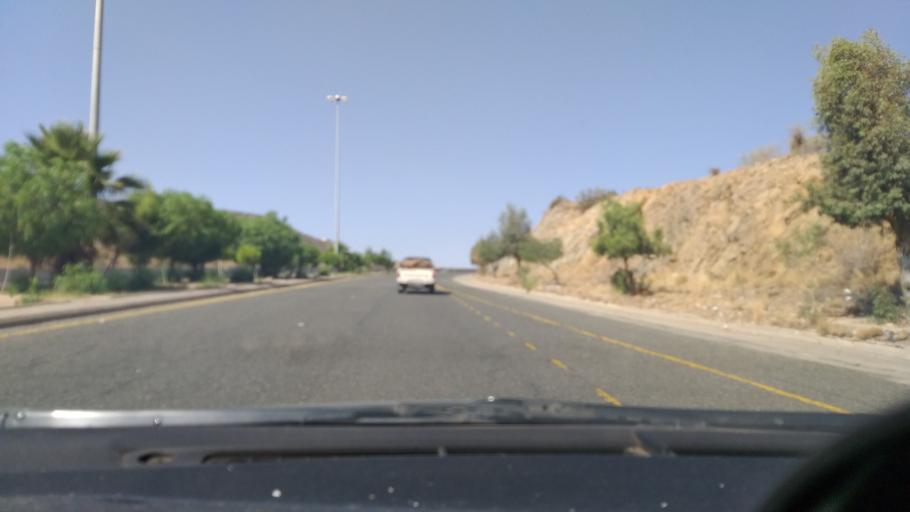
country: SA
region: Makkah
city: Ash Shafa
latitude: 21.0978
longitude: 40.3264
